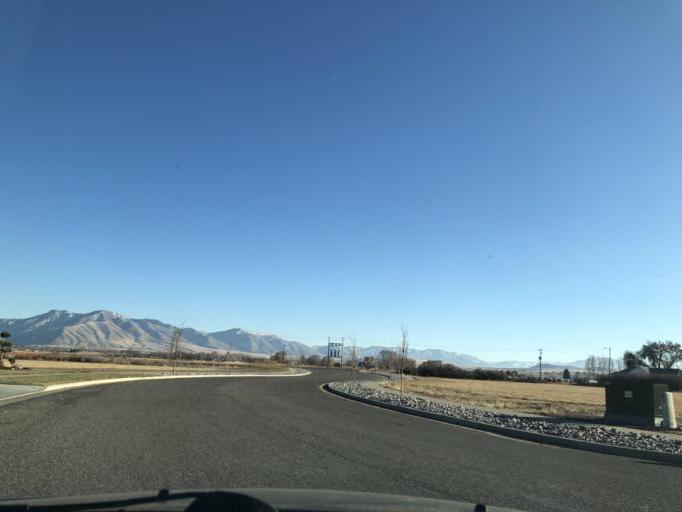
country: US
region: Utah
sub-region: Cache County
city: Wellsville
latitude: 41.6504
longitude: -111.9114
